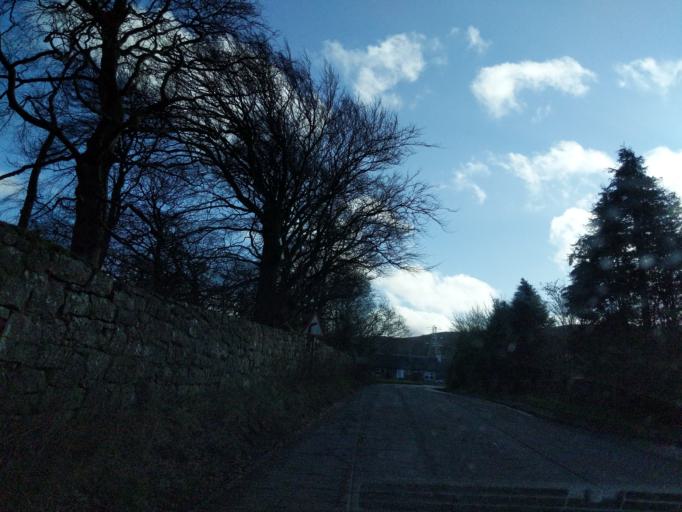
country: GB
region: Scotland
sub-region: Edinburgh
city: Ratho
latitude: 55.8945
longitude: -3.3823
